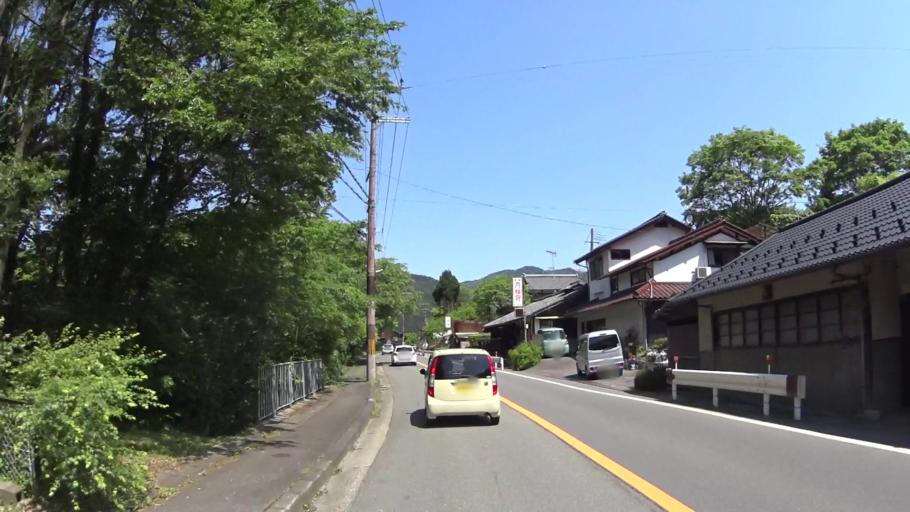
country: JP
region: Kyoto
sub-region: Kyoto-shi
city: Kamigyo-ku
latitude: 35.1050
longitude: 135.8245
